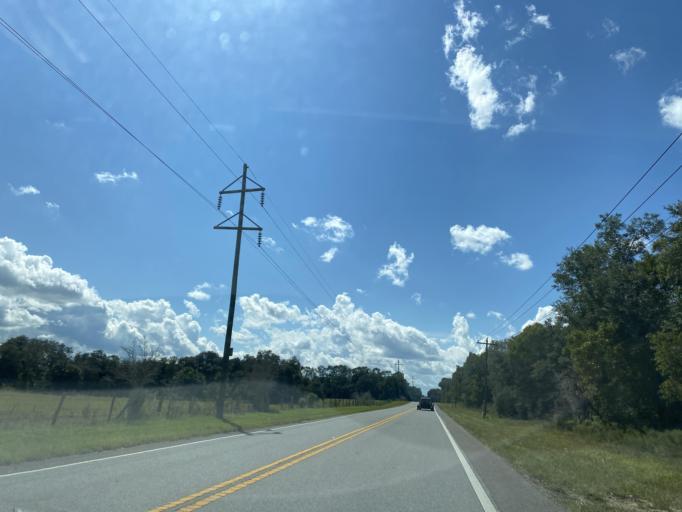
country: US
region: Florida
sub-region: Lake County
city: Umatilla
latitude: 28.9715
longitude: -81.5583
